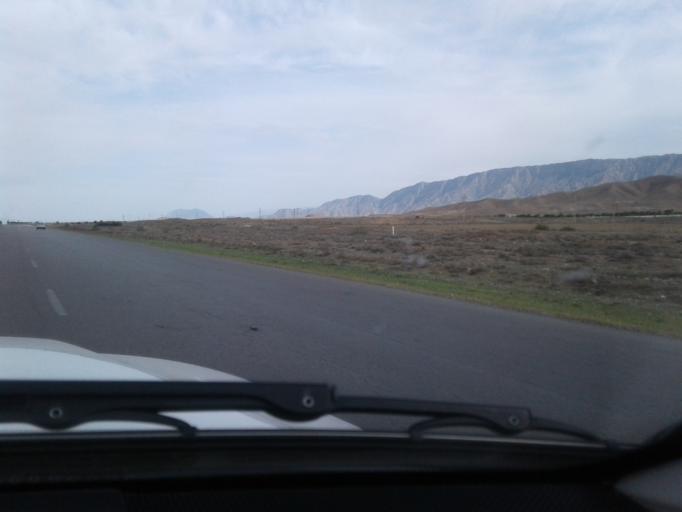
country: TM
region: Ahal
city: Baharly
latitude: 38.2392
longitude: 57.7698
